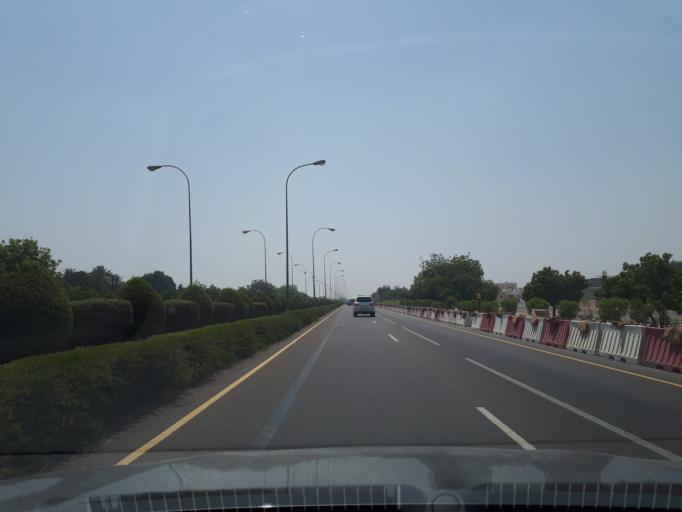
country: OM
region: Al Batinah
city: Al Sohar
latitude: 24.3935
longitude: 56.6887
